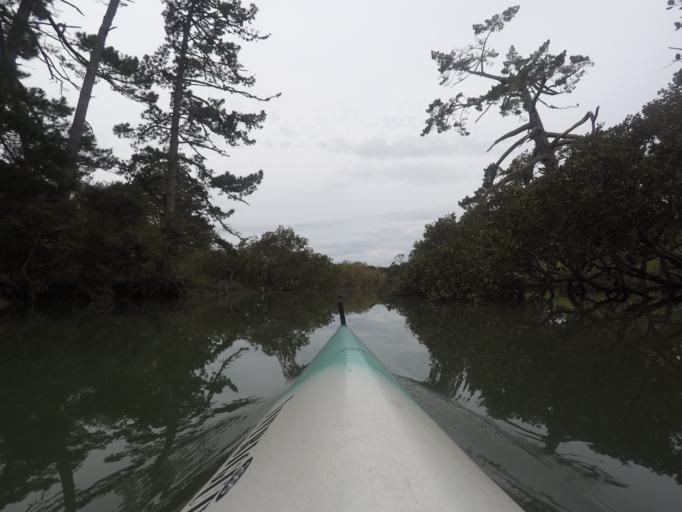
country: NZ
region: Auckland
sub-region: Auckland
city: Rothesay Bay
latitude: -36.6795
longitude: 174.7063
